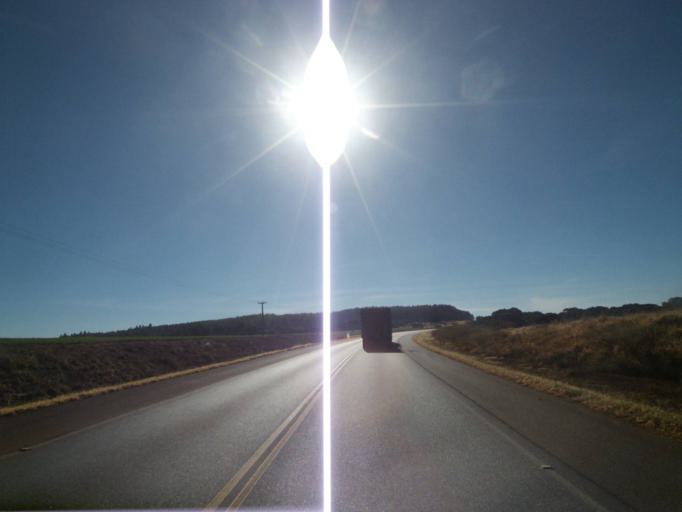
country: BR
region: Parana
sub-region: Tibagi
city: Tibagi
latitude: -24.4380
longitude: -50.4218
